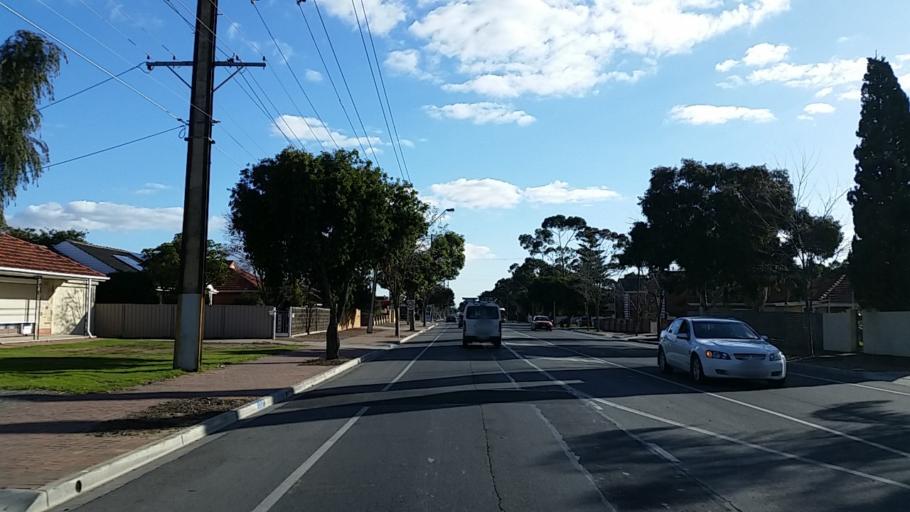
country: AU
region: South Australia
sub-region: Campbelltown
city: Paradise
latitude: -34.8762
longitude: 138.6776
